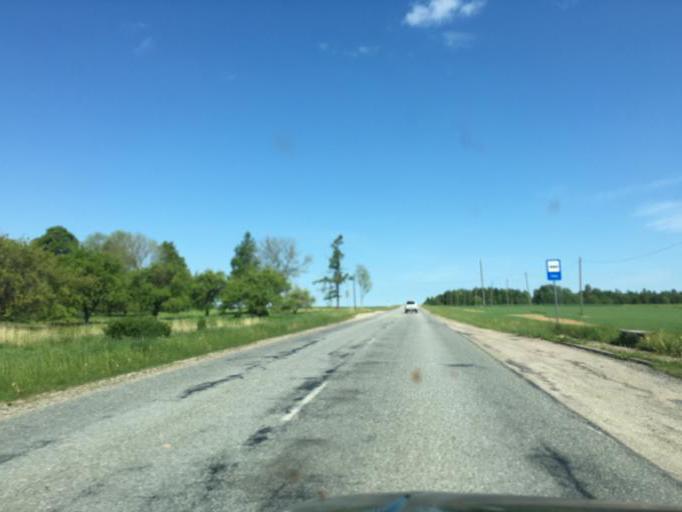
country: LV
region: Talsu Rajons
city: Valdemarpils
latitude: 57.3569
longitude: 22.4937
